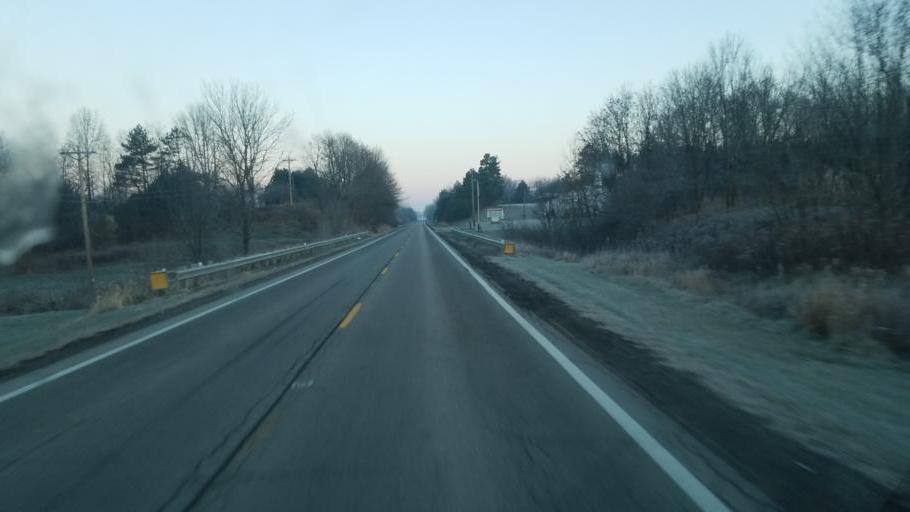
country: US
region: Ohio
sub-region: Wayne County
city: West Salem
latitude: 40.9490
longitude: -82.1094
